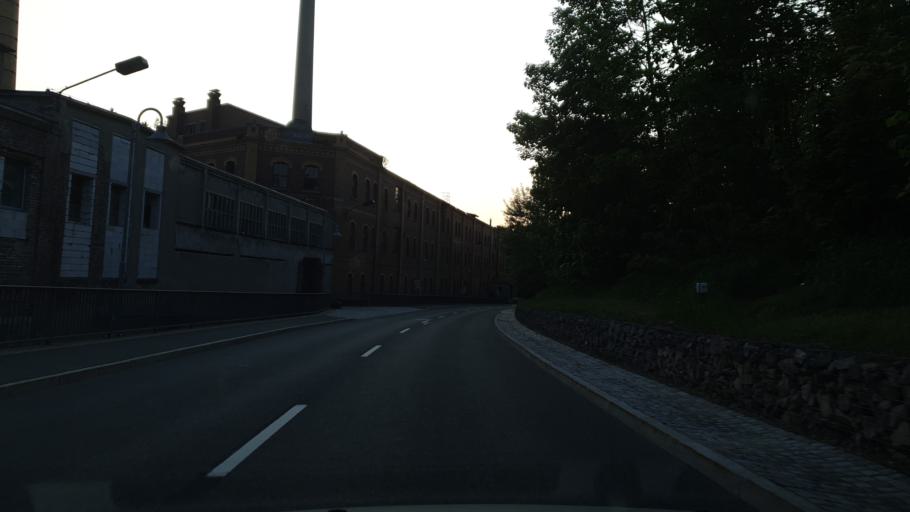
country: DE
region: Saxony
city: Tannenbergsthal
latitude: 50.4324
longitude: 12.4636
